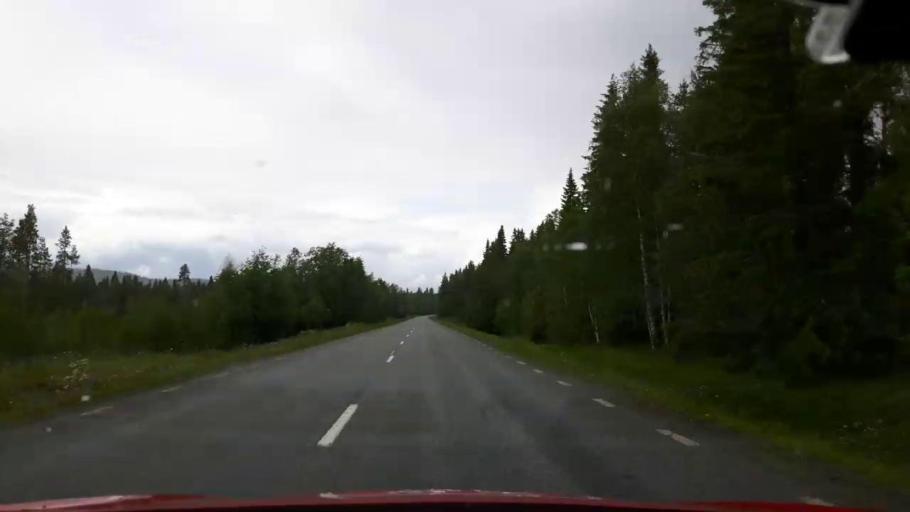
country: SE
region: Jaemtland
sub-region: Krokoms Kommun
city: Krokom
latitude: 63.4420
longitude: 14.1981
